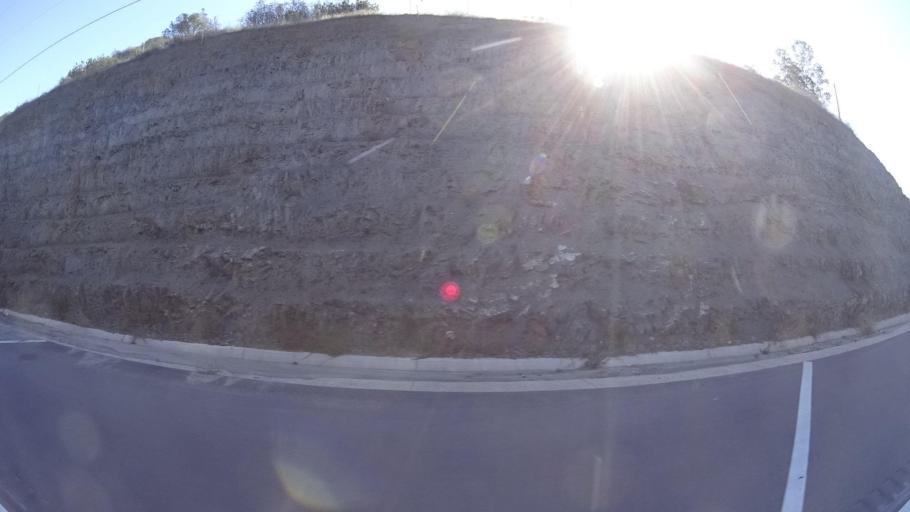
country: MX
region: Baja California
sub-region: Tijuana
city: El Nino
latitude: 32.6345
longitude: -116.7652
